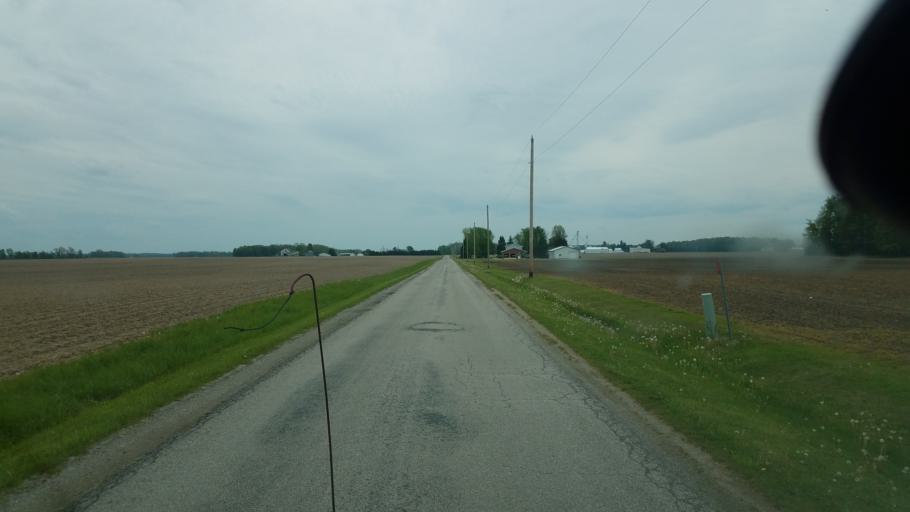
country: US
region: Ohio
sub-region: Huron County
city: Willard
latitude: 41.0200
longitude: -82.7988
